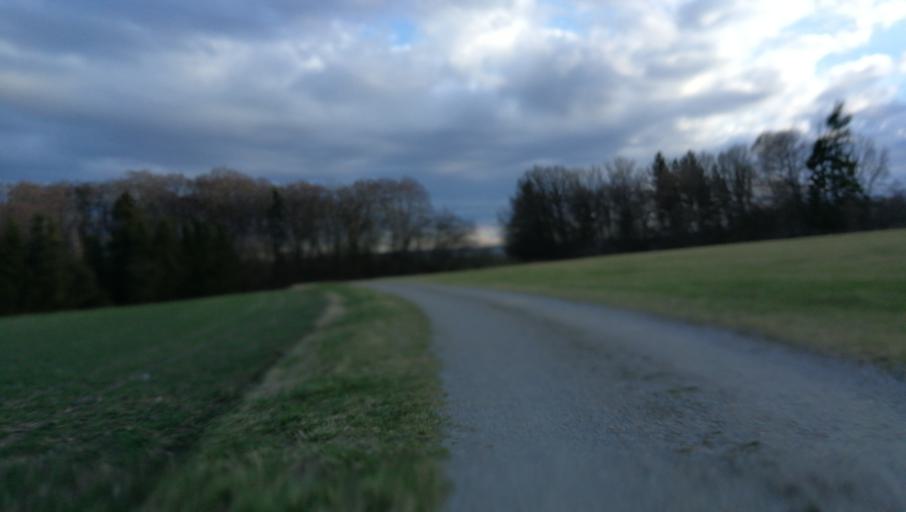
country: DE
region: Bavaria
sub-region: Upper Bavaria
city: Fuerstenfeldbruck
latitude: 48.1976
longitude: 11.2260
